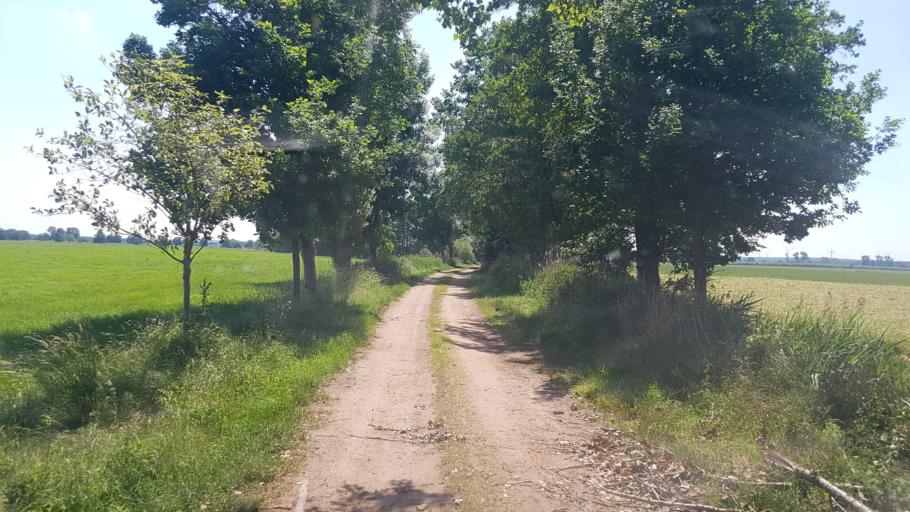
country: DE
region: Brandenburg
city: Schlieben
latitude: 51.7204
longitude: 13.3304
